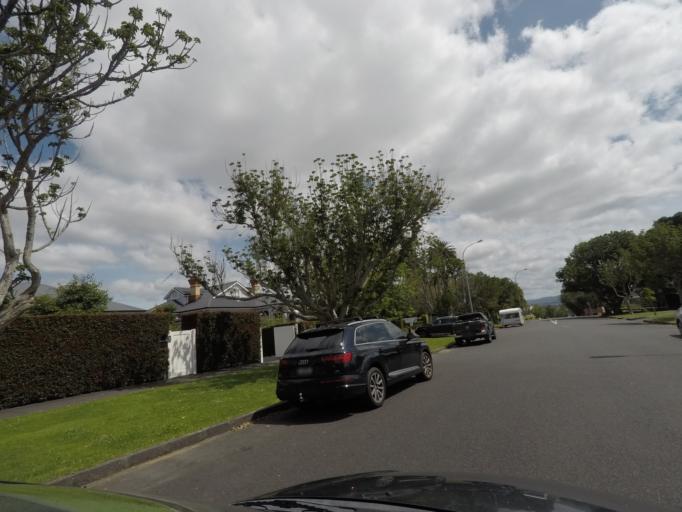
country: NZ
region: Auckland
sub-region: Auckland
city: Auckland
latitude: -36.8485
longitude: 174.7278
